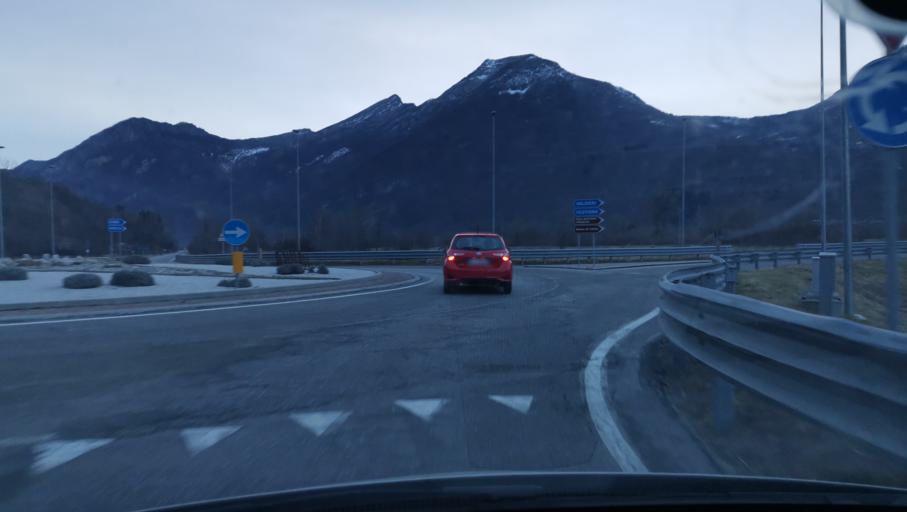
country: IT
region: Piedmont
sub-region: Provincia di Cuneo
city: Valloriate
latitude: 44.3129
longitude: 7.3446
